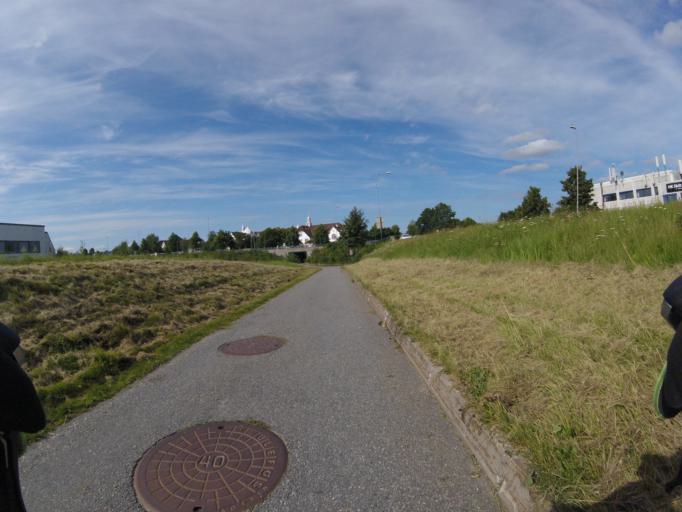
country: NO
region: Akershus
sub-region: Skedsmo
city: Lillestrom
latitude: 59.9778
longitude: 11.0010
